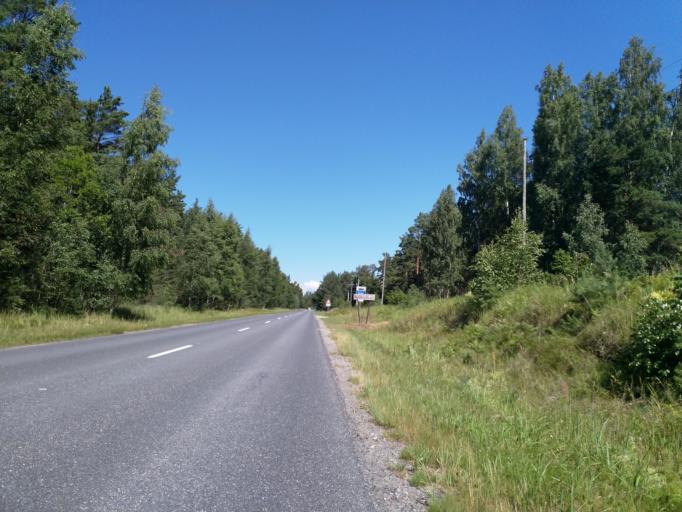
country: LV
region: Dundaga
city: Dundaga
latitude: 57.7327
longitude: 22.5800
